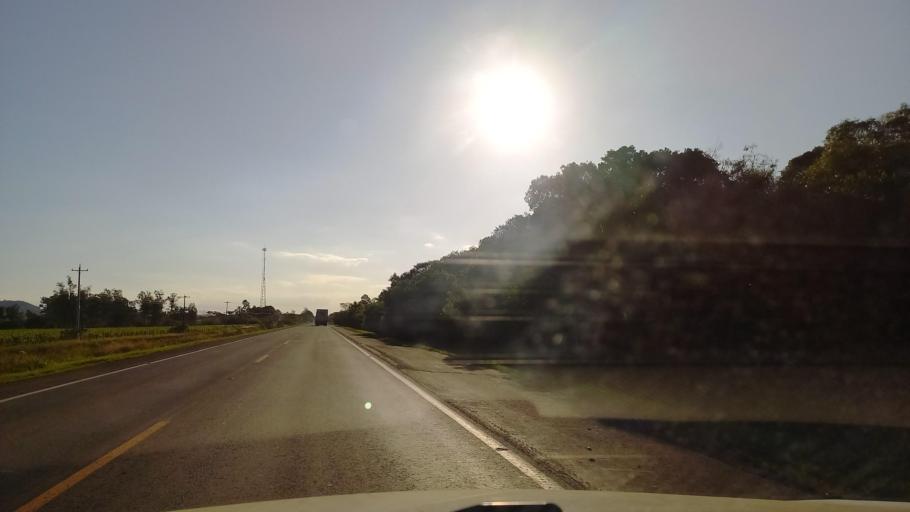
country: BR
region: Rio Grande do Sul
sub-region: Venancio Aires
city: Venancio Aires
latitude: -29.6674
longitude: -52.0452
